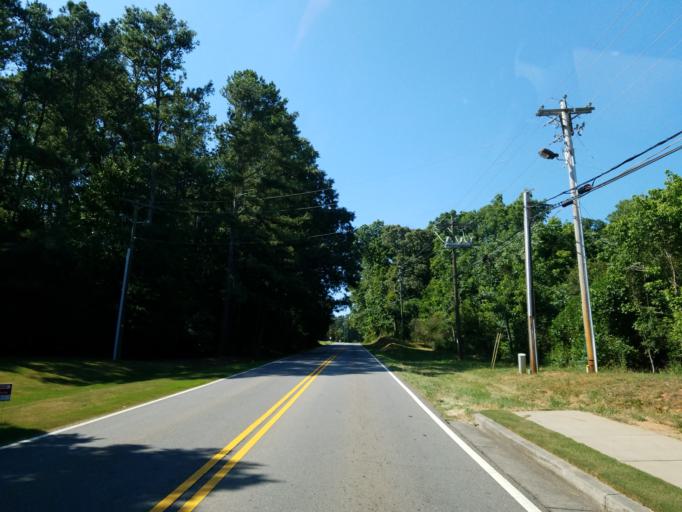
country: US
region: Georgia
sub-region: Fulton County
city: Milton
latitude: 34.1353
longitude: -84.3437
